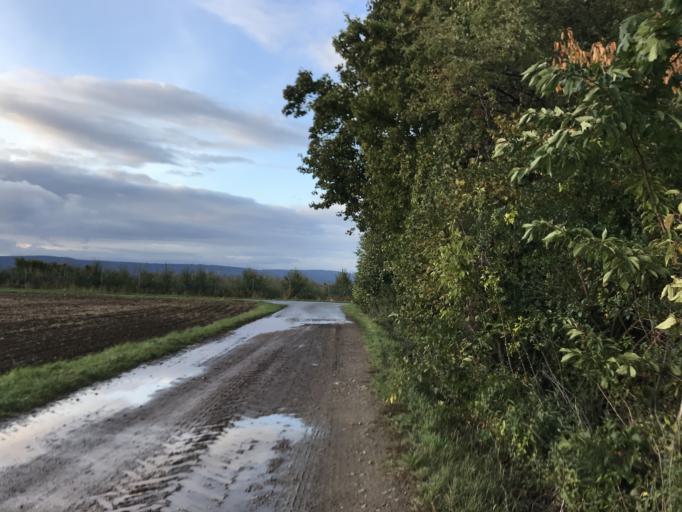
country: DE
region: Rheinland-Pfalz
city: Wackernheim
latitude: 49.9706
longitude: 8.0980
